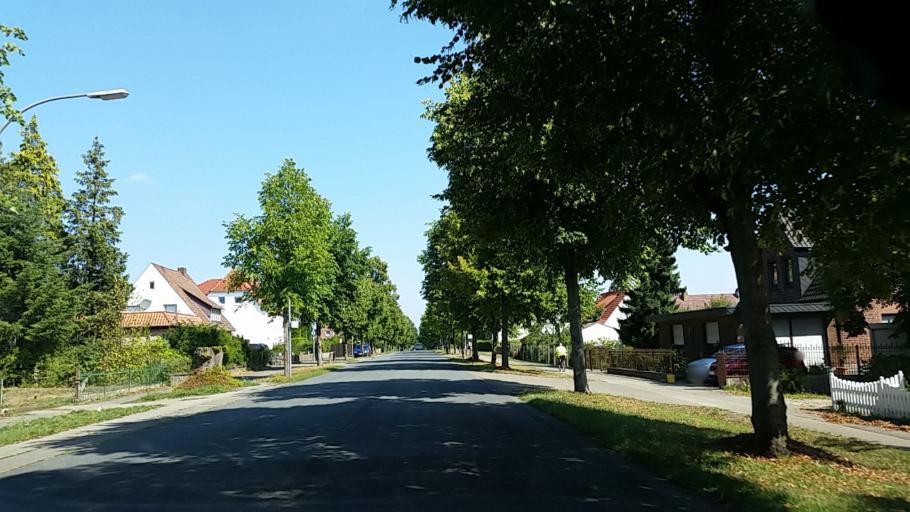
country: DE
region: Lower Saxony
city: Uelzen
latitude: 52.9272
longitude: 10.5284
